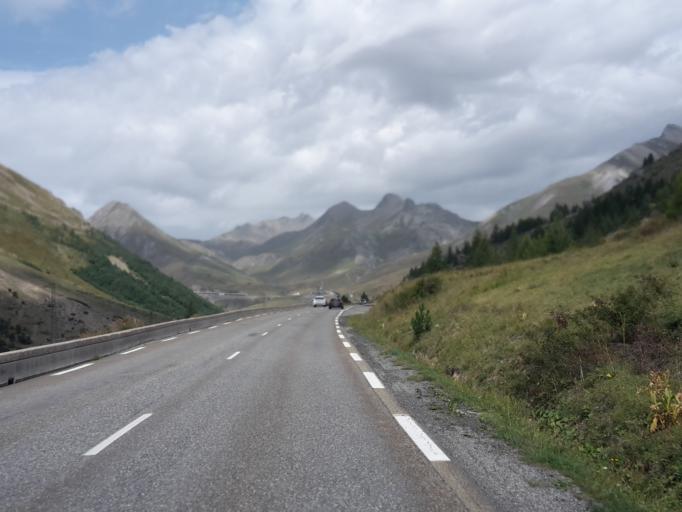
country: FR
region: Provence-Alpes-Cote d'Azur
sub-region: Departement des Hautes-Alpes
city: Le Monetier-les-Bains
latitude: 45.0256
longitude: 6.4512
